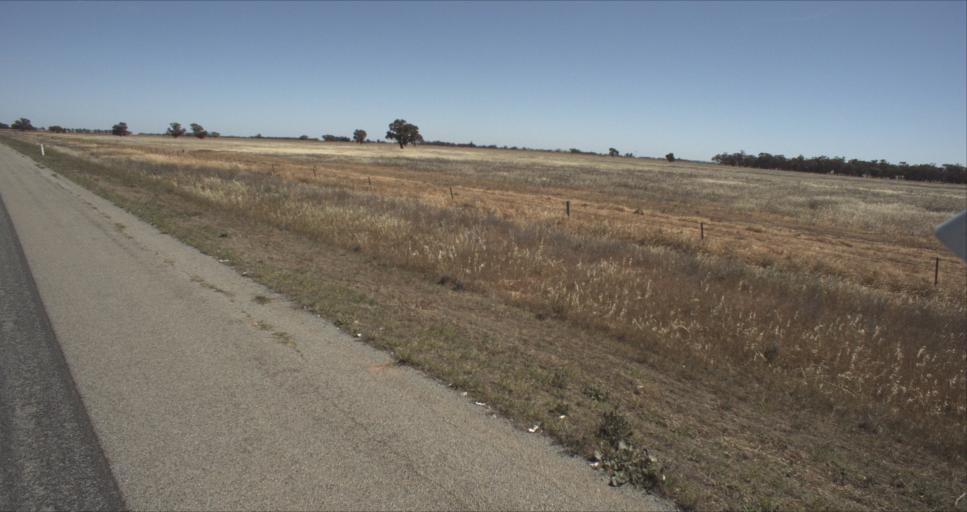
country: AU
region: New South Wales
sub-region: Leeton
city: Leeton
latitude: -34.5831
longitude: 146.3057
